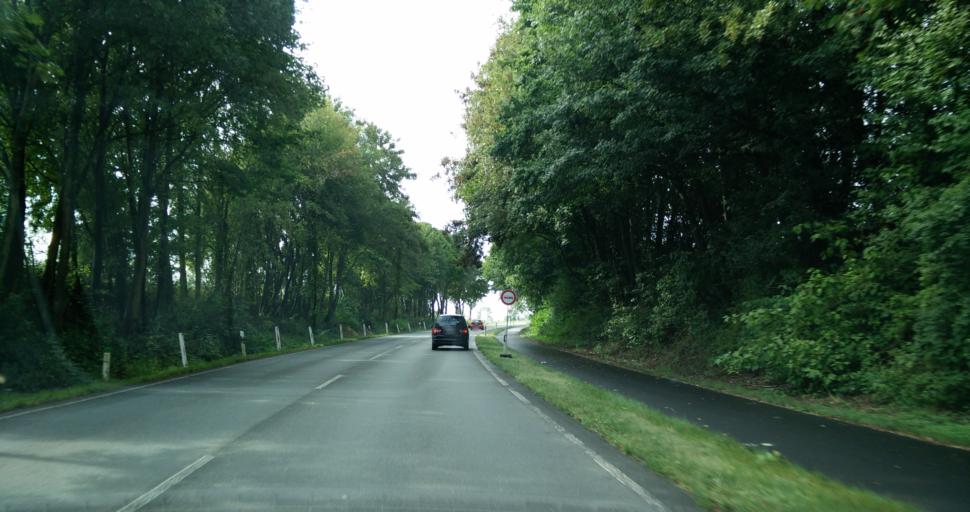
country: DE
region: North Rhine-Westphalia
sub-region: Regierungsbezirk Dusseldorf
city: Mettmann
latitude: 51.2344
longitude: 6.9618
